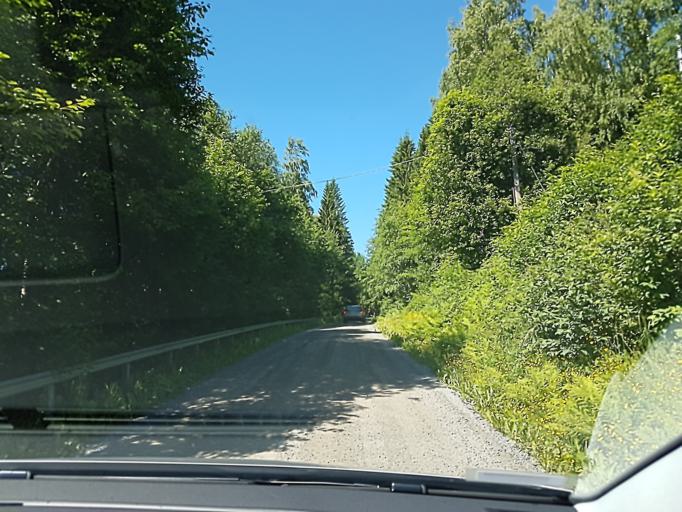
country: SE
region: Vaesternorrland
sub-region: OErnskoeldsviks Kommun
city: Bjasta
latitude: 63.0666
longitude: 18.4272
